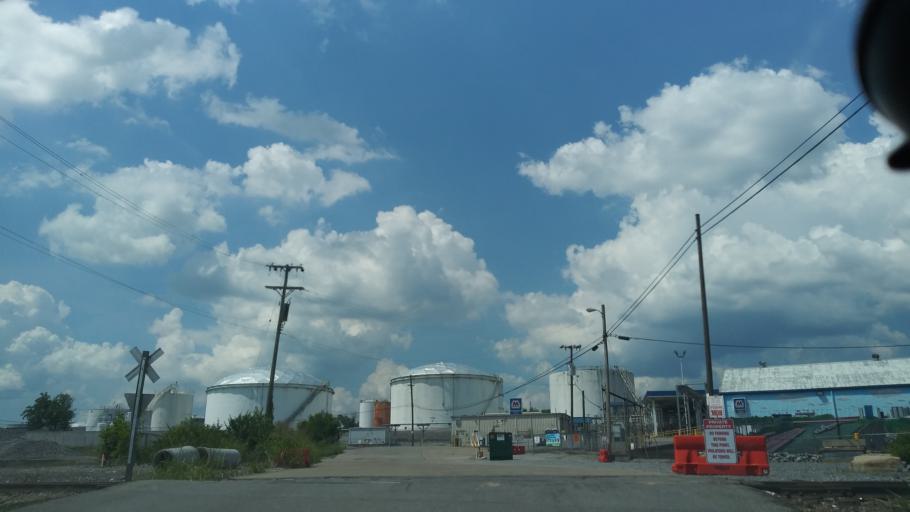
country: US
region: Tennessee
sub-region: Davidson County
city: Nashville
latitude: 36.1638
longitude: -86.8492
